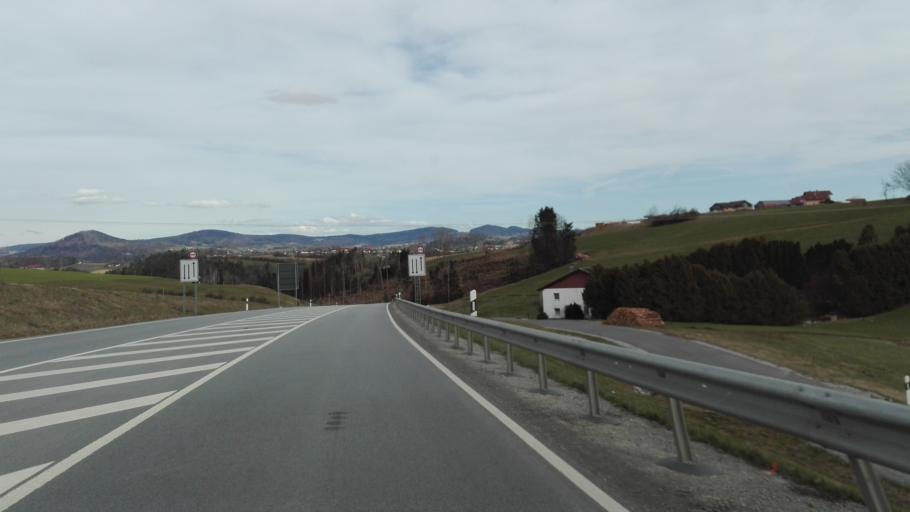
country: DE
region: Bavaria
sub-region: Lower Bavaria
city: Thyrnau
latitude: 48.6251
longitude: 13.5579
